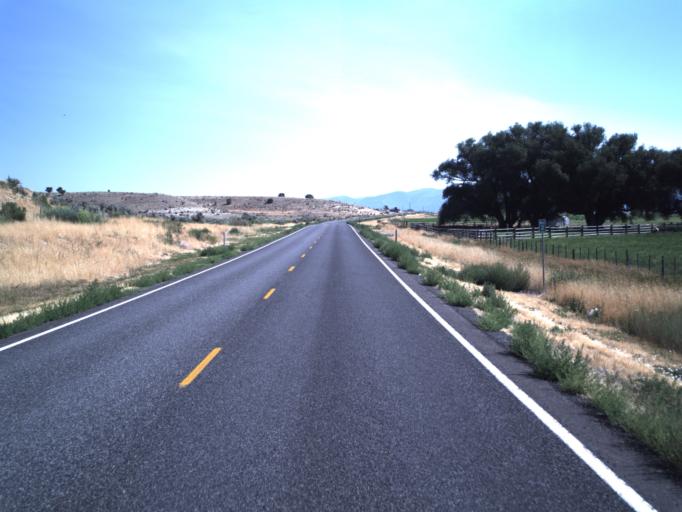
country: US
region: Utah
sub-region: Sanpete County
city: Moroni
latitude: 39.5327
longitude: -111.5429
